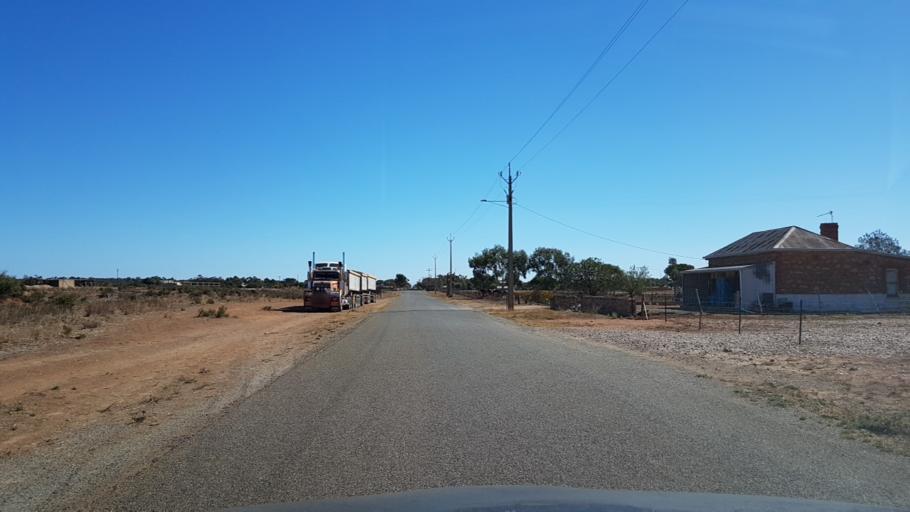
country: AU
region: South Australia
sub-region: Peterborough
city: Peterborough
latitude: -32.9719
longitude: 138.8524
